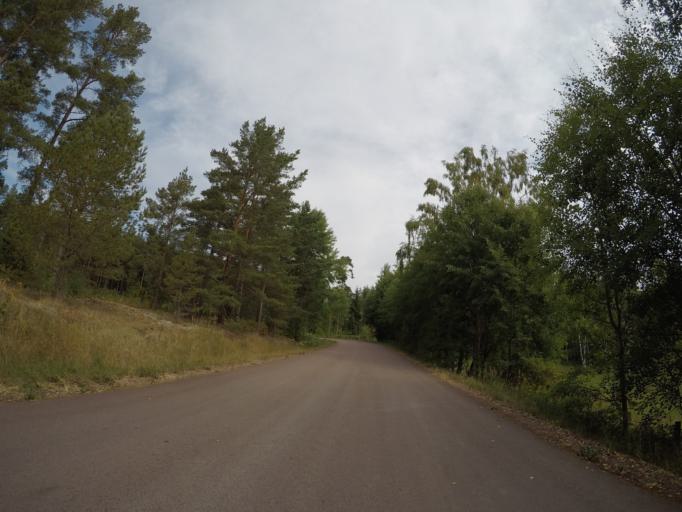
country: AX
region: Alands landsbygd
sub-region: Finstroem
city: Finstroem
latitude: 60.2541
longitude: 19.9145
